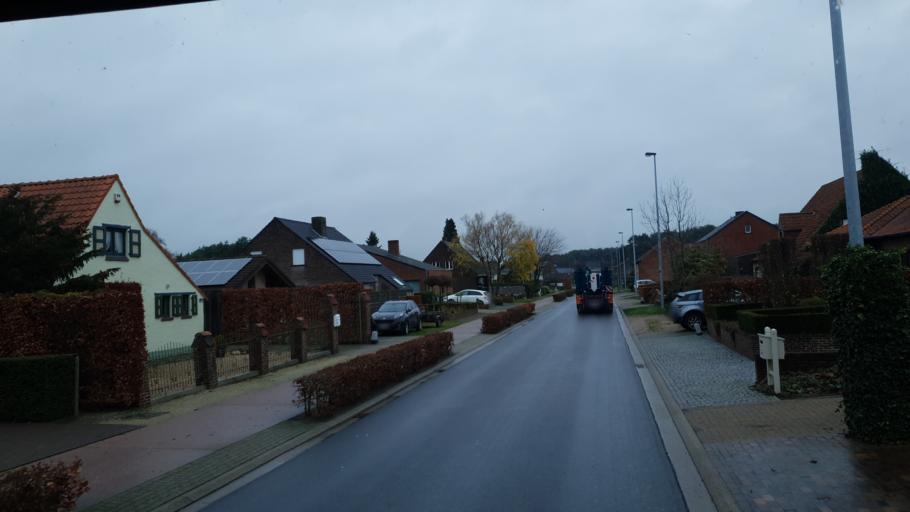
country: BE
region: Flanders
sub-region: Provincie Antwerpen
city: Olen
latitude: 51.1606
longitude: 4.8856
